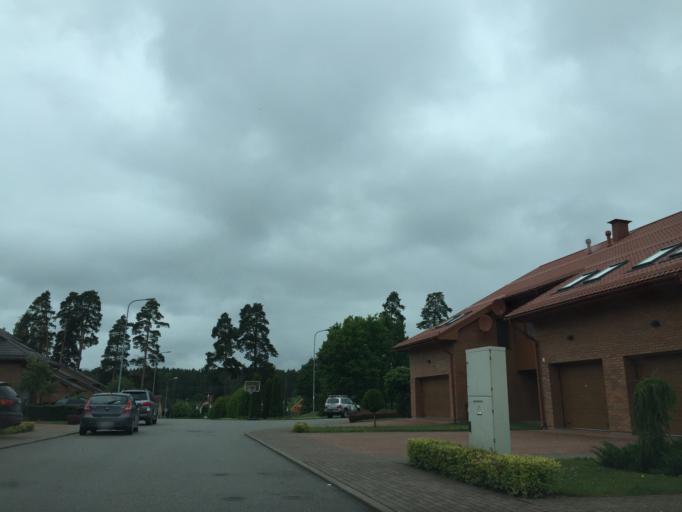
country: LV
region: Riga
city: Jaunciems
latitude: 57.0181
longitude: 24.2157
